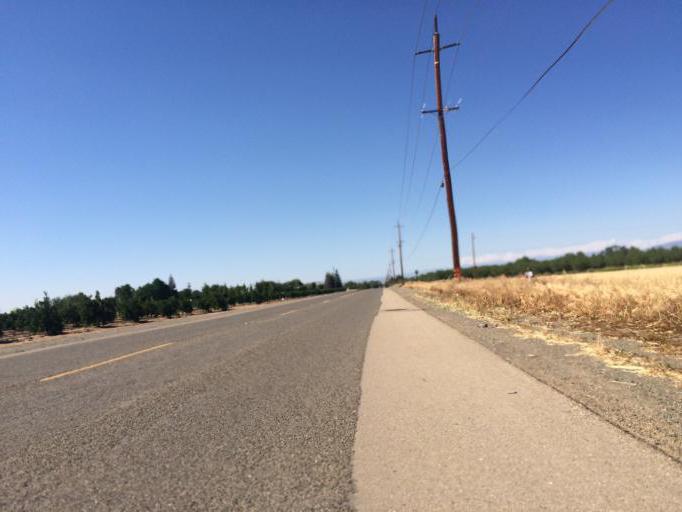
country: US
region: California
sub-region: Fresno County
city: Sanger
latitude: 36.7744
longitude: -119.6101
